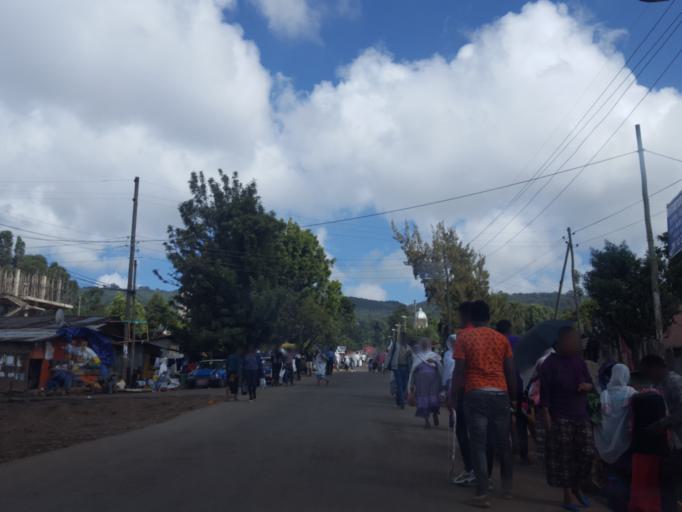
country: ET
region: Adis Abeba
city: Addis Ababa
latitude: 9.0678
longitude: 38.7608
